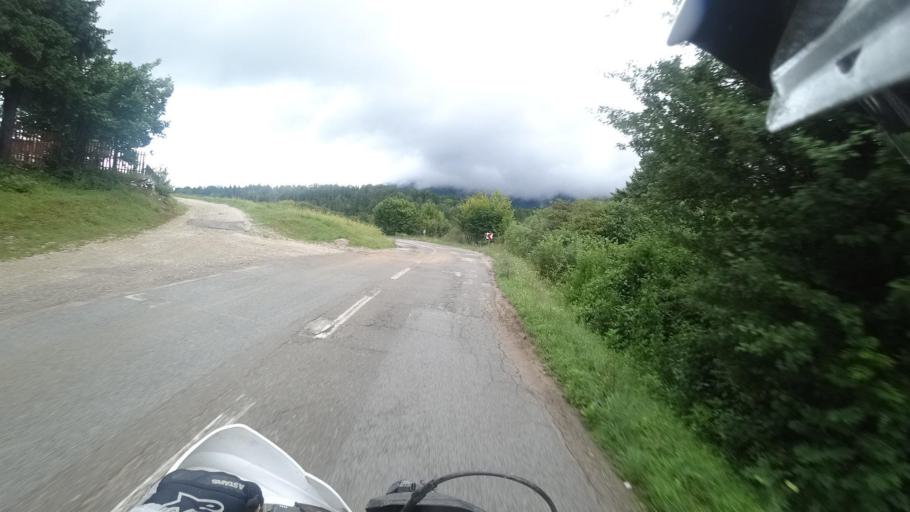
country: HR
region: Karlovacka
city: Plaski
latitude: 45.0128
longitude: 15.4195
